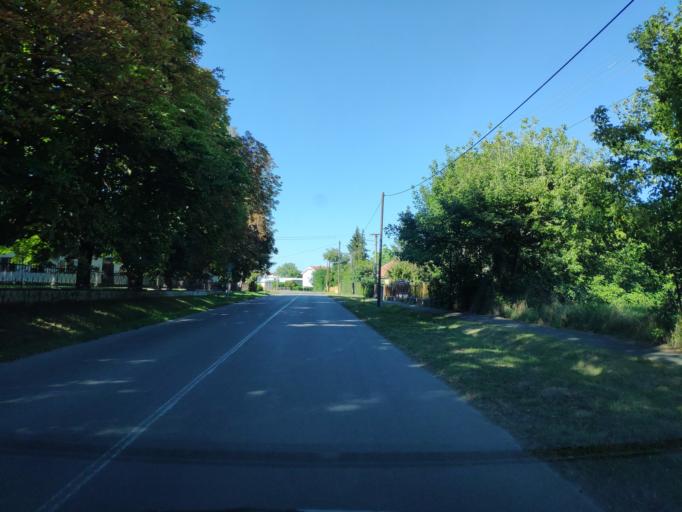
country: SK
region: Kosicky
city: Trebisov
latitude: 48.5819
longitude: 21.8491
